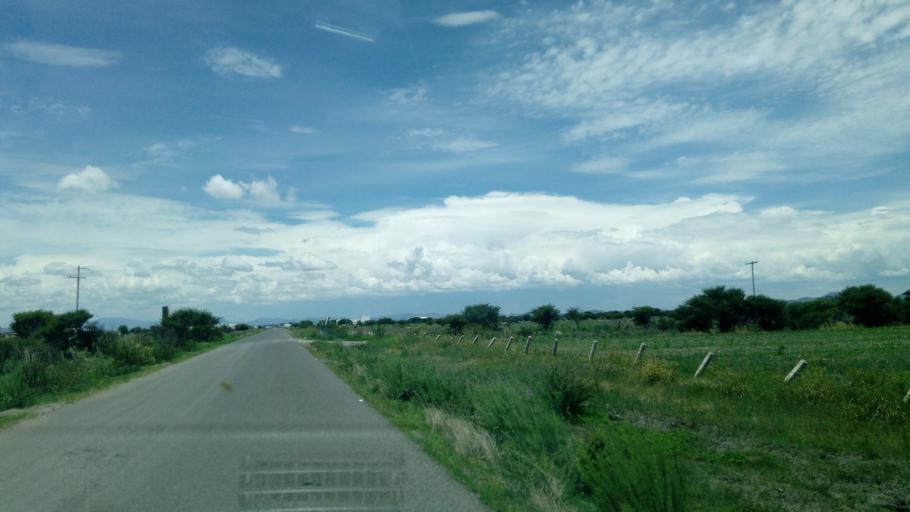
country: MX
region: Durango
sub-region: Durango
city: Jose Refugio Salcido
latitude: 24.1598
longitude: -104.5059
